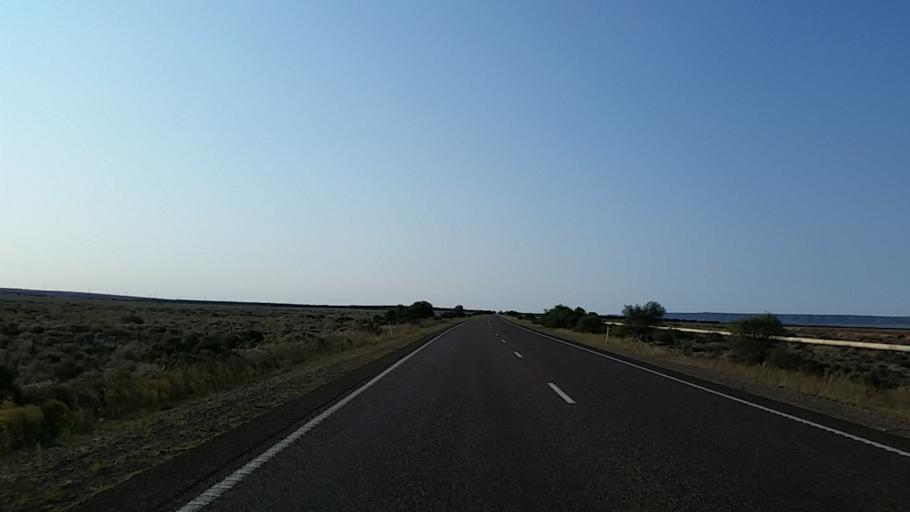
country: AU
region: South Australia
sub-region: Whyalla
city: Whyalla
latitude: -32.8517
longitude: 137.5512
